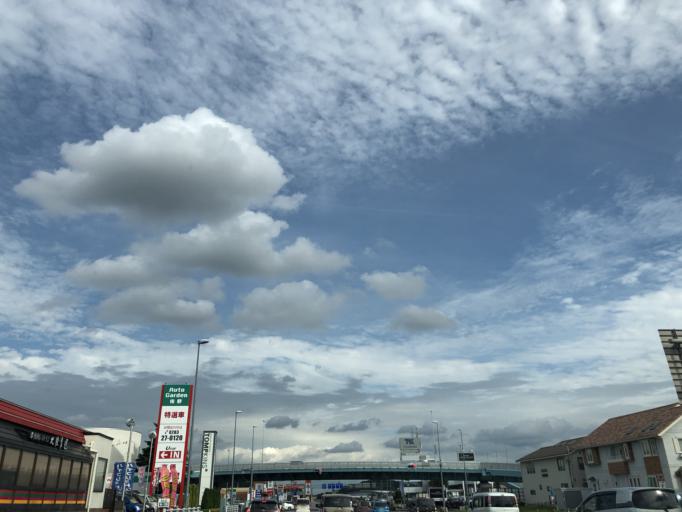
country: JP
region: Tochigi
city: Sano
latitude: 36.2965
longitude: 139.6029
